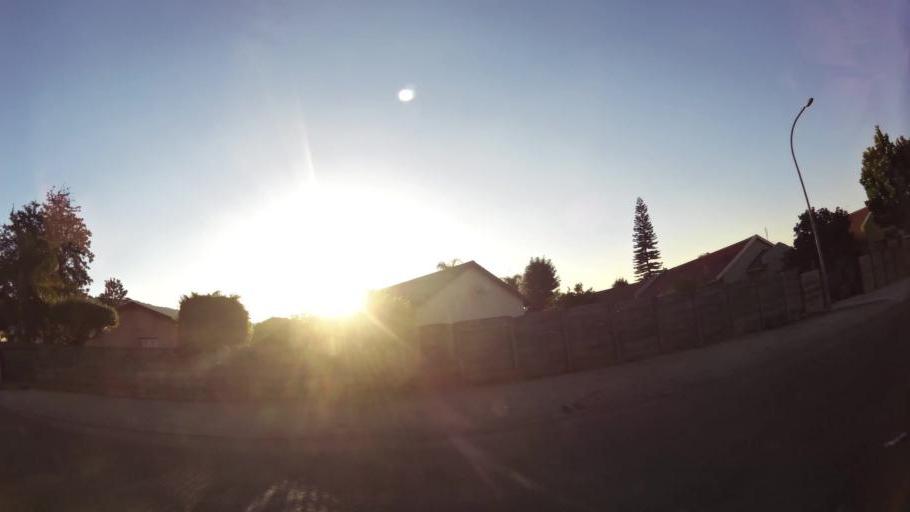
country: ZA
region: North-West
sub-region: Bojanala Platinum District Municipality
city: Rustenburg
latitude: -25.6405
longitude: 27.2061
